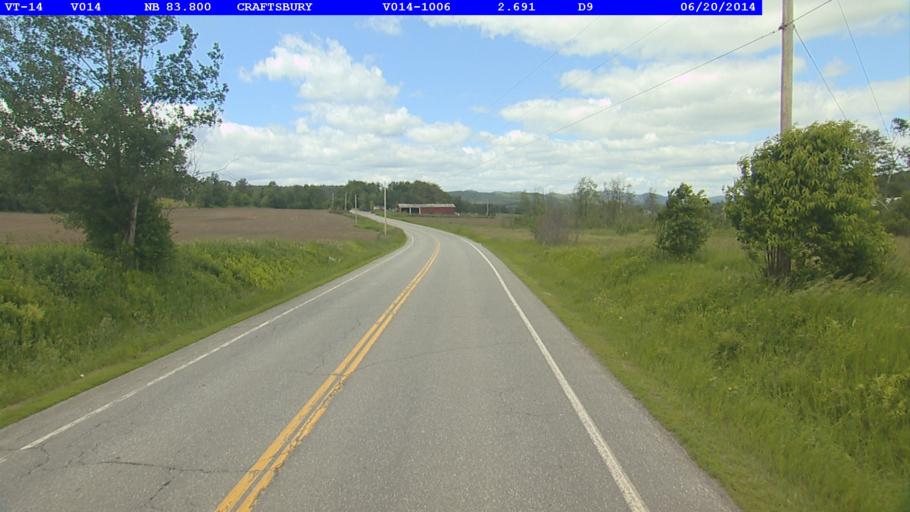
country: US
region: Vermont
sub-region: Caledonia County
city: Hardwick
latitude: 44.6318
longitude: -72.3924
